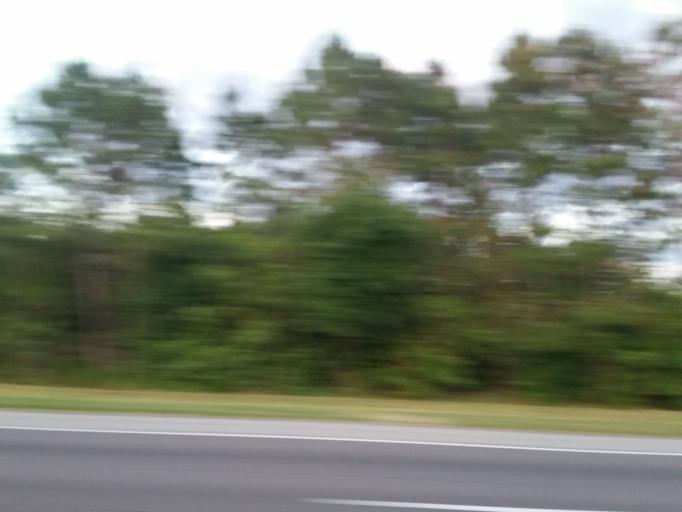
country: US
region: Florida
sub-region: Hillsborough County
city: Sun City Center
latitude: 27.7307
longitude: -82.3829
